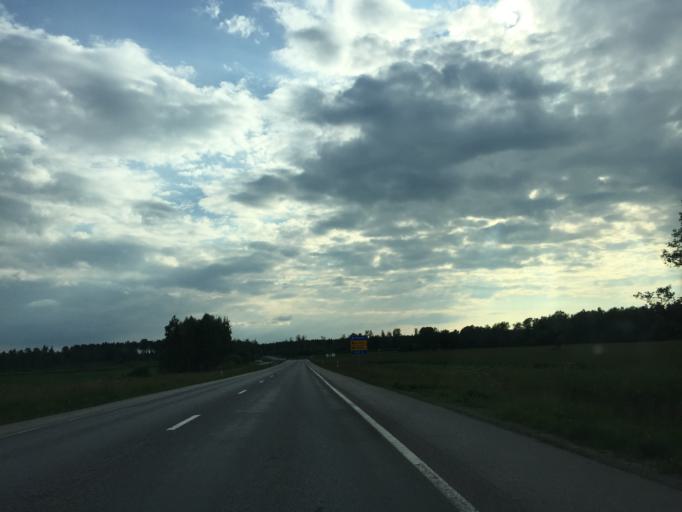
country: SE
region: OErebro
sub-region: Lindesbergs Kommun
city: Fellingsbro
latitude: 59.3443
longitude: 15.5875
